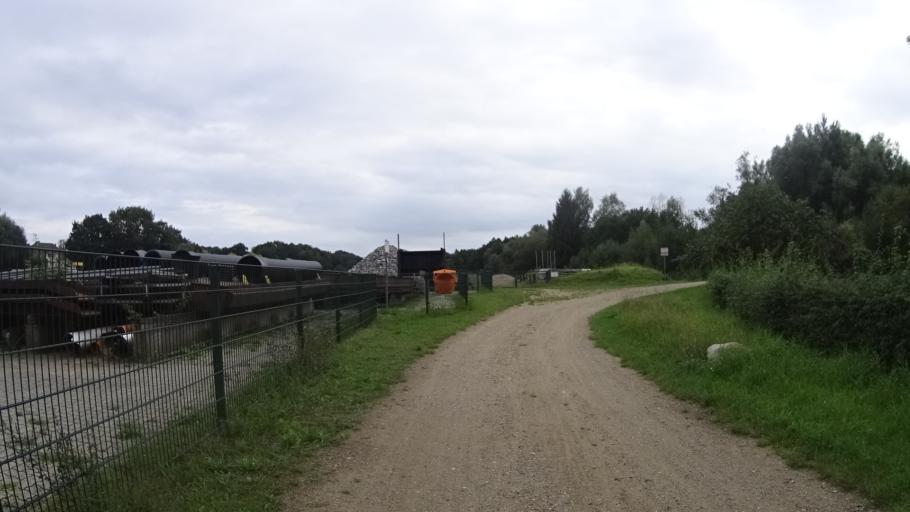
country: DE
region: Schleswig-Holstein
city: Panten
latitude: 53.6712
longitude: 10.6362
